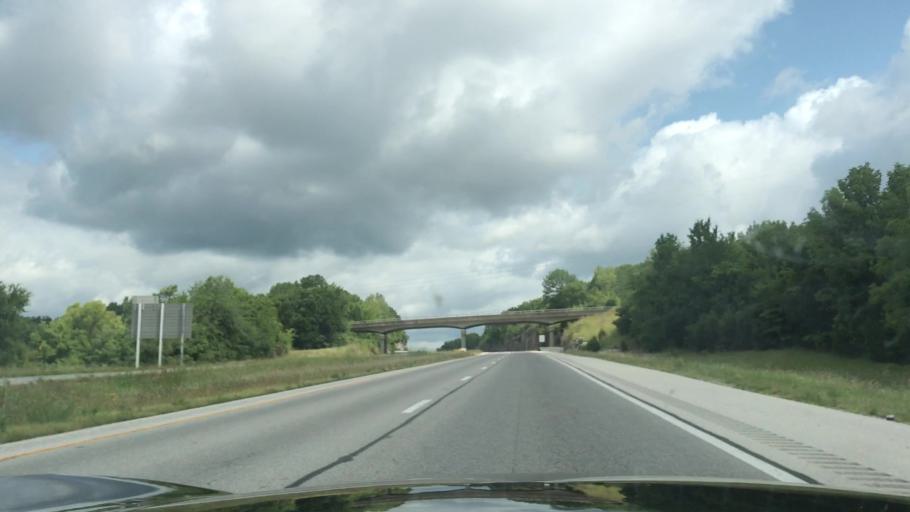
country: US
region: Kentucky
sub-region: Warren County
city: Bowling Green
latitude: 37.0007
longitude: -86.5061
